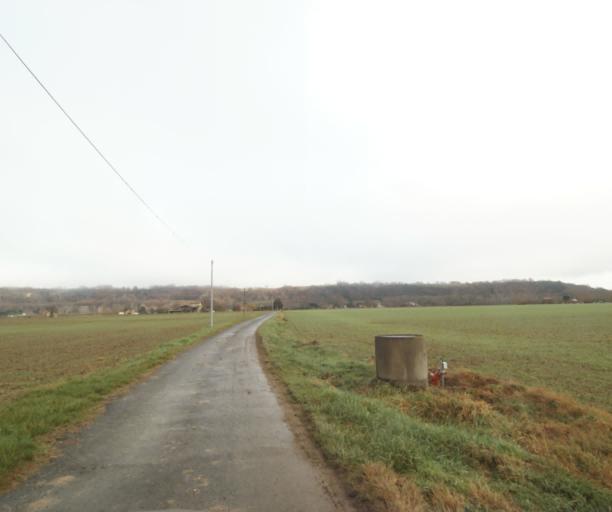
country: FR
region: Midi-Pyrenees
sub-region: Departement du Tarn-et-Garonne
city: Nohic
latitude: 43.8864
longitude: 1.4699
